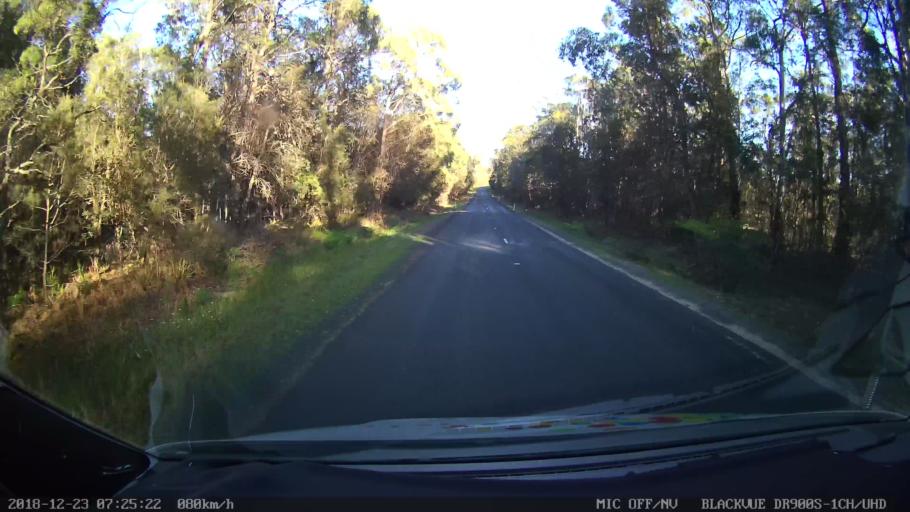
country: AU
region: New South Wales
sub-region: Armidale Dumaresq
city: Enmore
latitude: -30.4990
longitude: 152.2114
